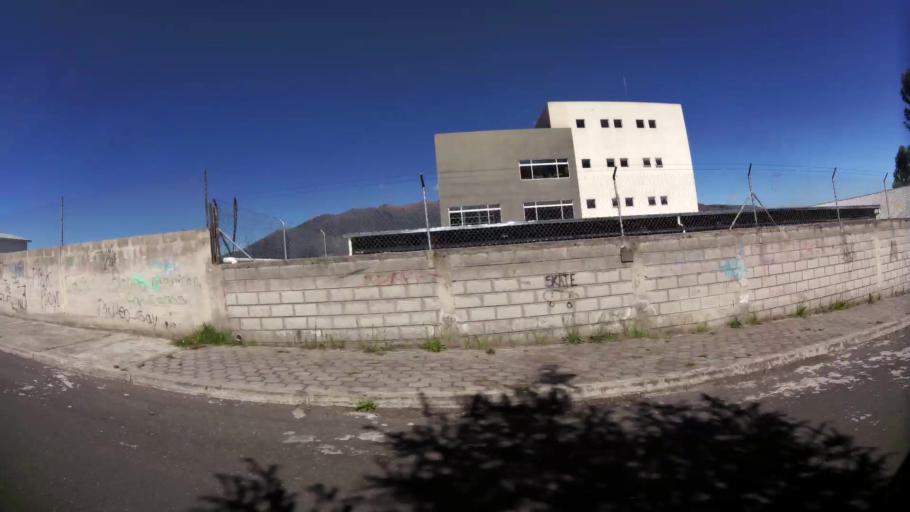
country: EC
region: Pichincha
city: Quito
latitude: -0.1228
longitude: -78.4779
